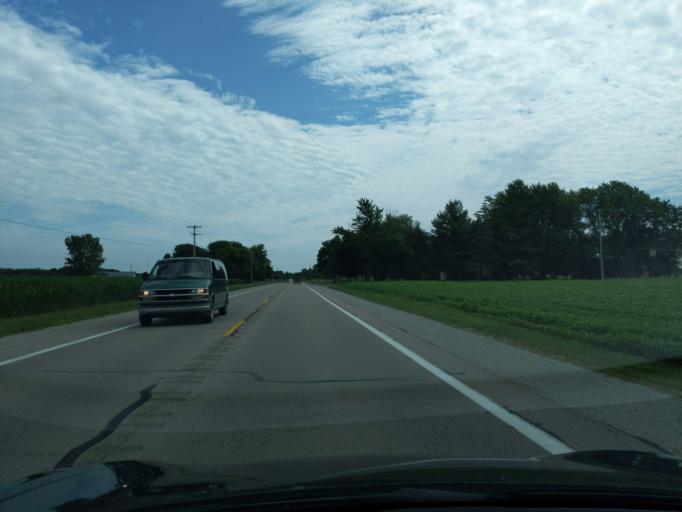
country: US
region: Michigan
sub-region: Gratiot County
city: Breckenridge
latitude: 43.4080
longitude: -84.3860
